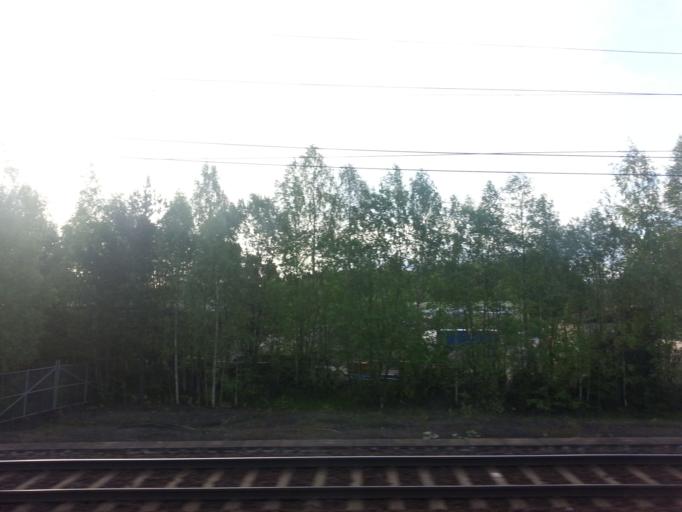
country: NO
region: Akershus
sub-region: Skedsmo
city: Lillestrom
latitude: 59.9636
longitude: 11.0655
